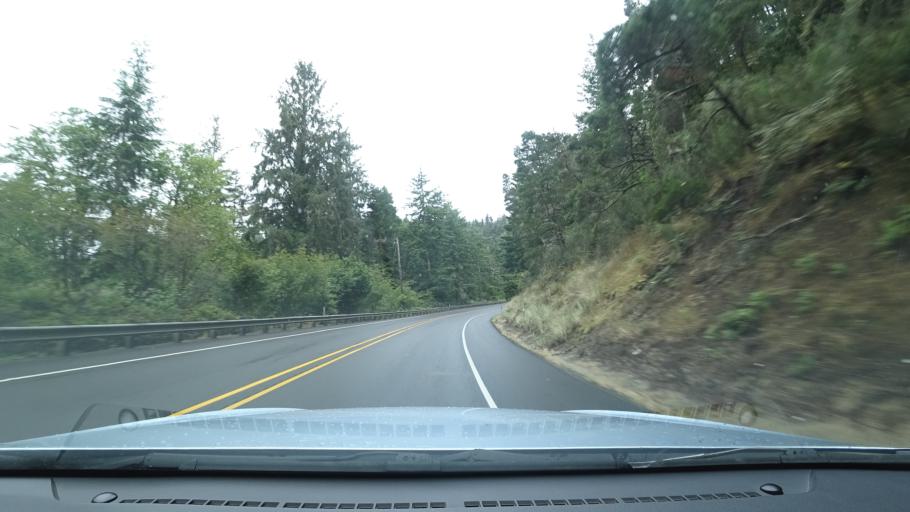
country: US
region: Oregon
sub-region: Lane County
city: Dunes City
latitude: 43.8834
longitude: -124.1221
